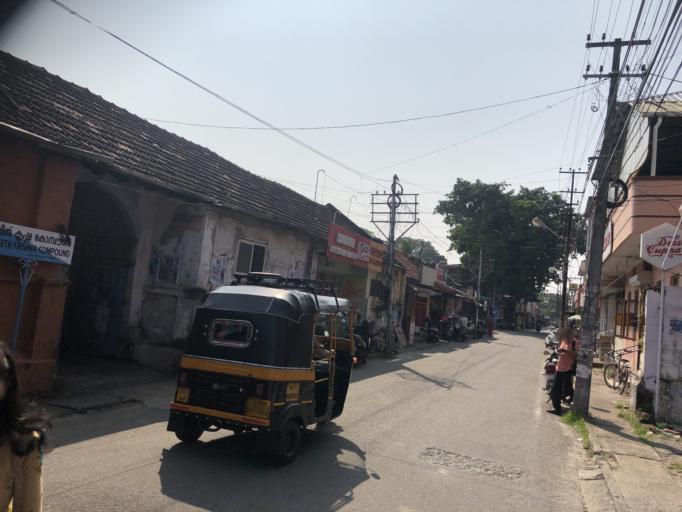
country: IN
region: Kerala
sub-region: Ernakulam
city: Cochin
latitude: 9.9578
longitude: 76.2550
